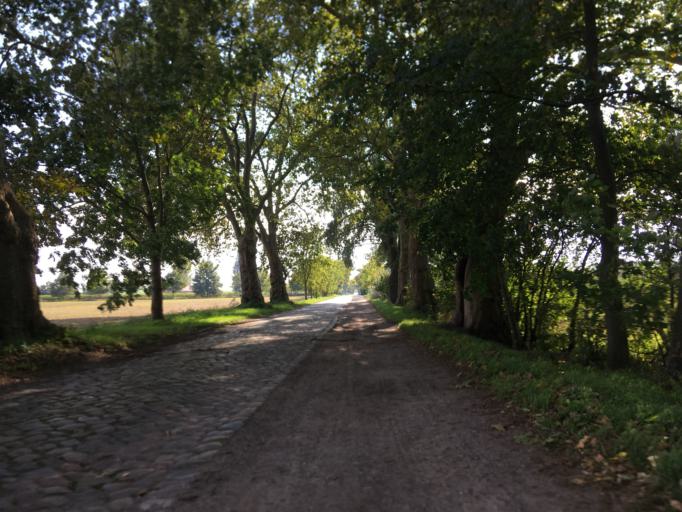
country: DE
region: Brandenburg
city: Altlandsberg
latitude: 52.5603
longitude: 13.7299
